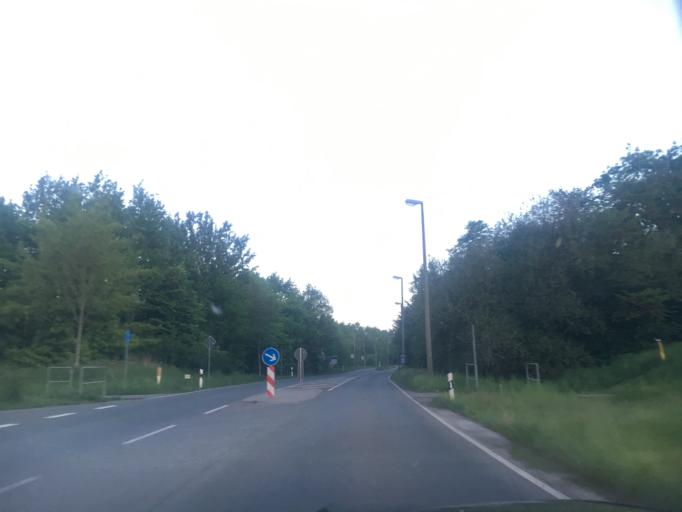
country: DE
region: Thuringia
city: Gera
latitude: 50.8442
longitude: 12.0778
